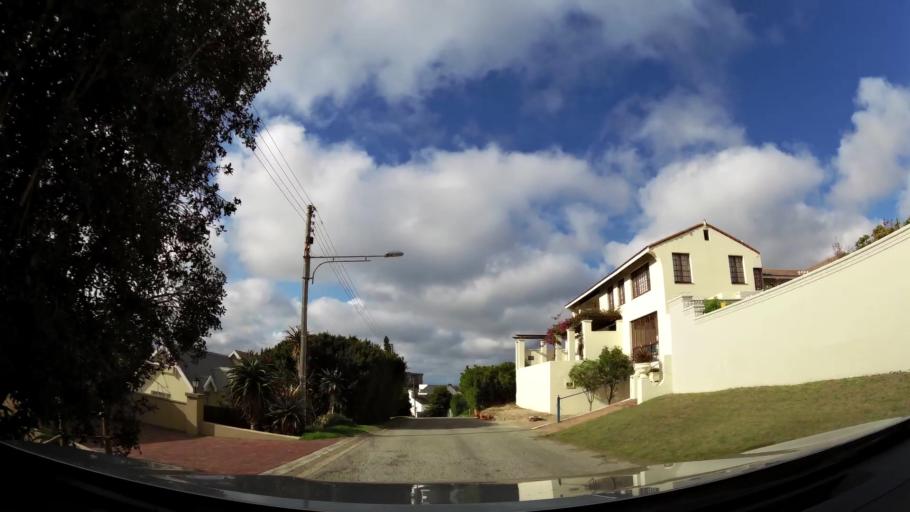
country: ZA
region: Western Cape
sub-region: Eden District Municipality
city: Plettenberg Bay
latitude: -34.0709
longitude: 23.3714
